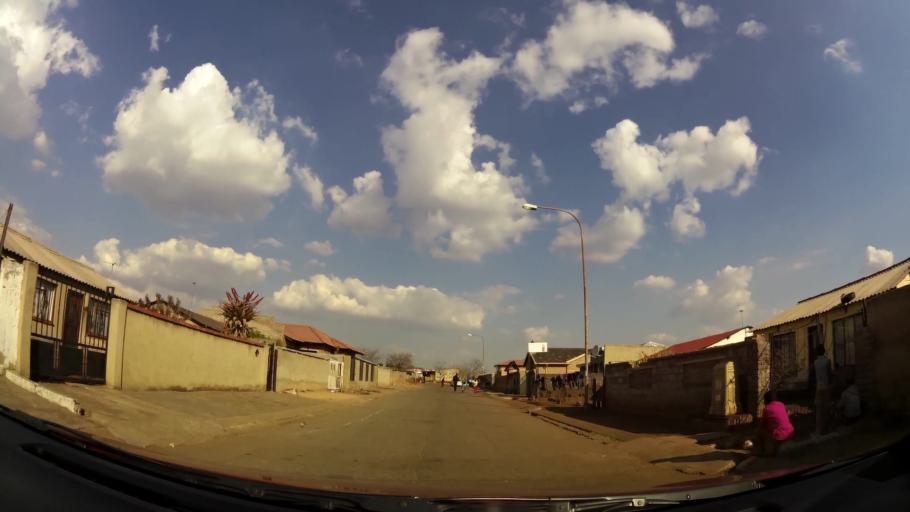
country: ZA
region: Gauteng
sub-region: City of Johannesburg Metropolitan Municipality
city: Soweto
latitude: -26.2283
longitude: 27.8685
